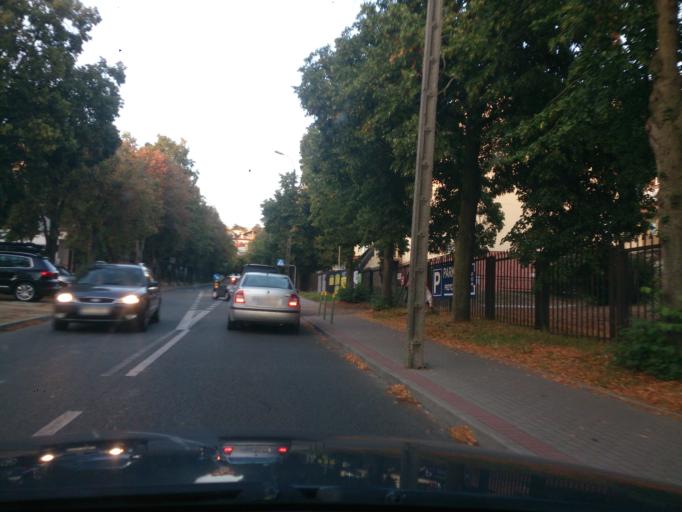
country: PL
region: Pomeranian Voivodeship
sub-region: Gdynia
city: Gdynia
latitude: 54.4882
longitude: 18.5486
